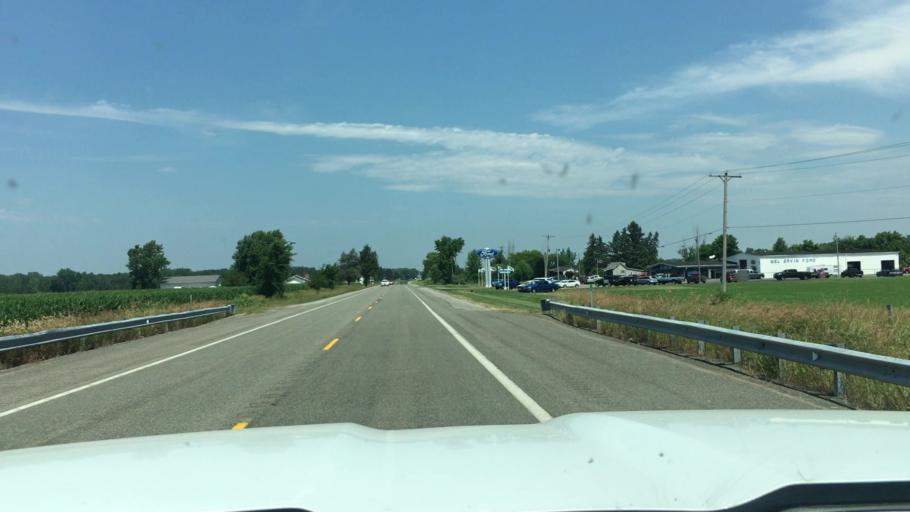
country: US
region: Michigan
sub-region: Saginaw County
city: Chesaning
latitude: 43.1913
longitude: -84.1691
